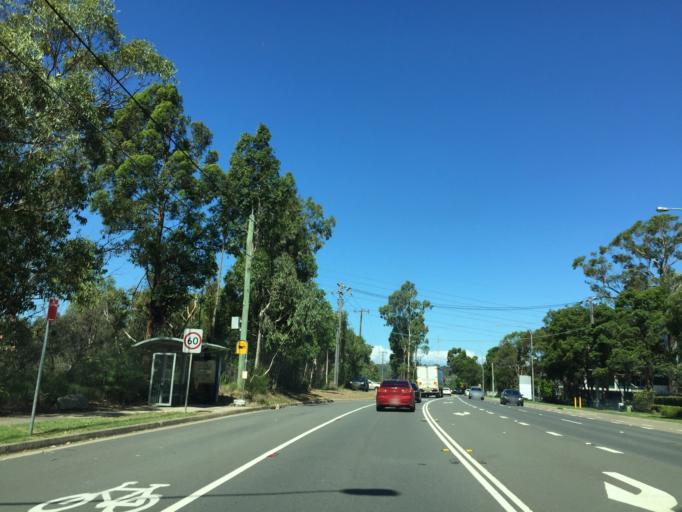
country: AU
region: New South Wales
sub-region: Ryde
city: East Ryde
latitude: -33.7956
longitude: 151.1441
